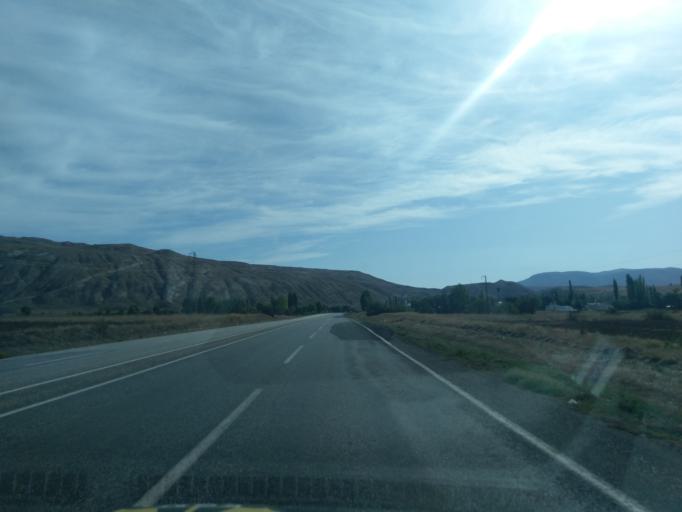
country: TR
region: Sivas
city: Zara
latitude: 39.8619
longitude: 37.8162
